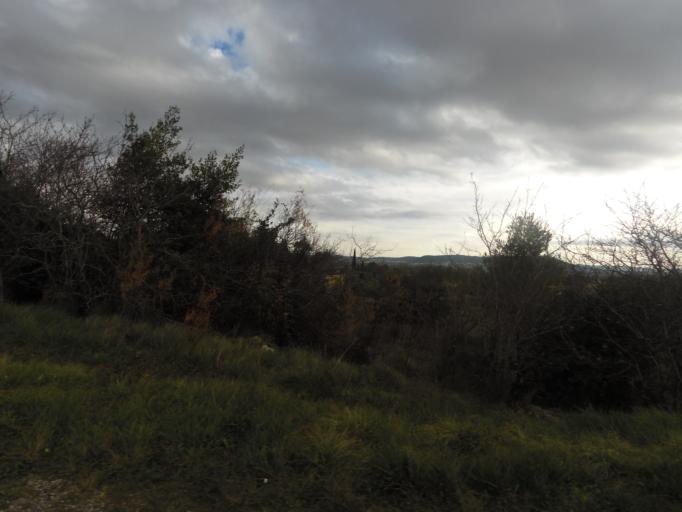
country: FR
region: Languedoc-Roussillon
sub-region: Departement du Gard
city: Clarensac
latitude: 43.8317
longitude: 4.2021
